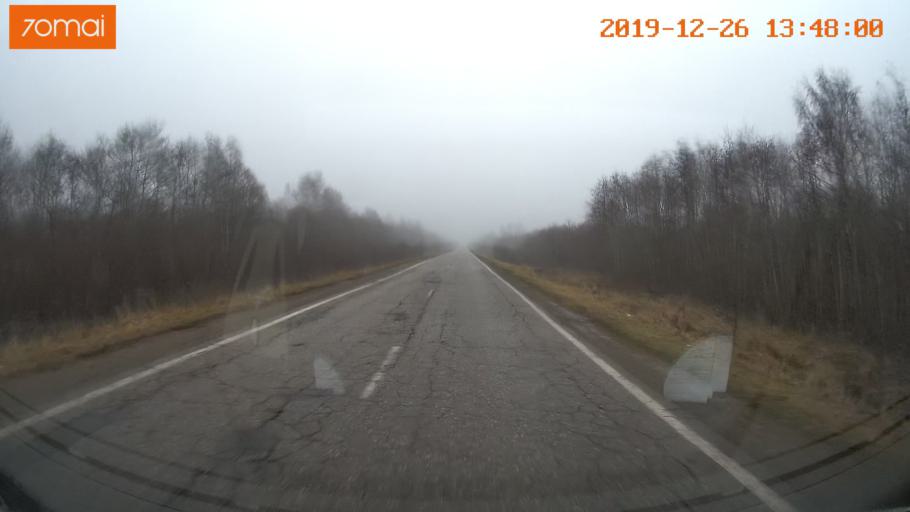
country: RU
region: Vologda
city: Sheksna
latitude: 58.6801
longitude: 38.5415
